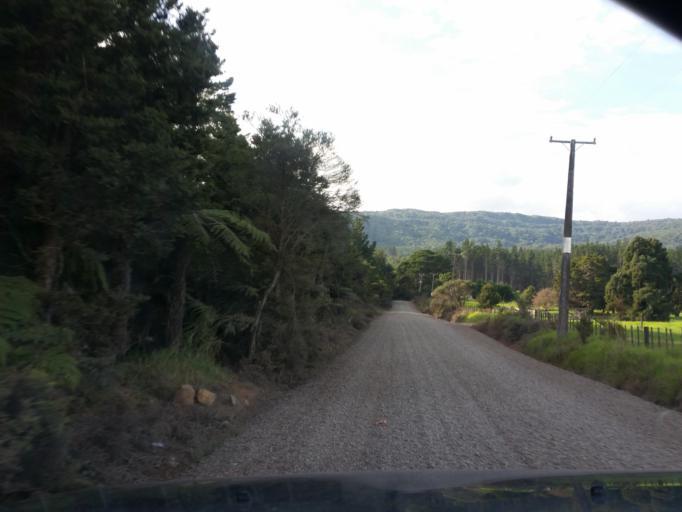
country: NZ
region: Northland
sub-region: Kaipara District
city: Dargaville
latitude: -35.7724
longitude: 173.7164
